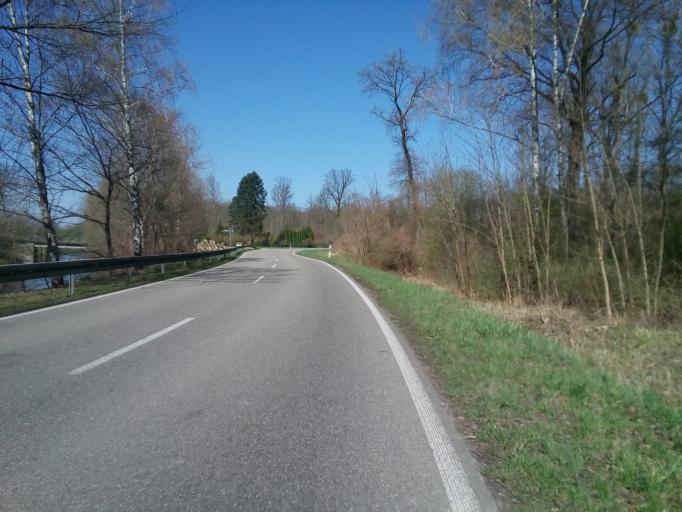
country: DE
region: Baden-Wuerttemberg
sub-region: Freiburg Region
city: Rheinau
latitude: 48.6739
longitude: 7.9130
